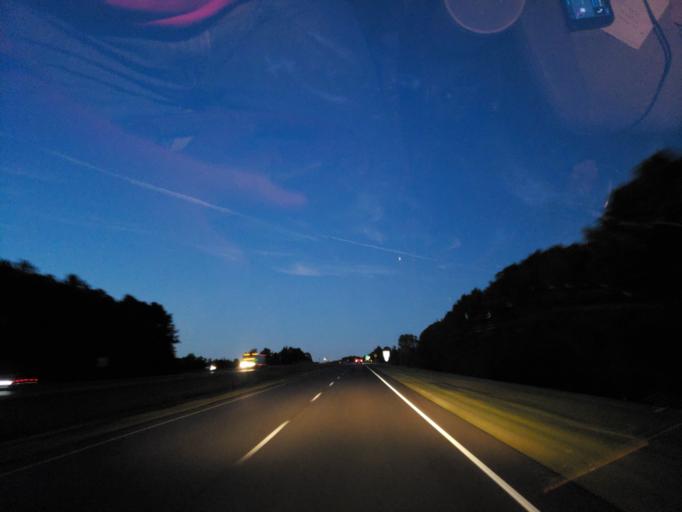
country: US
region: Mississippi
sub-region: Clarke County
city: Quitman
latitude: 32.0363
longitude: -88.6797
